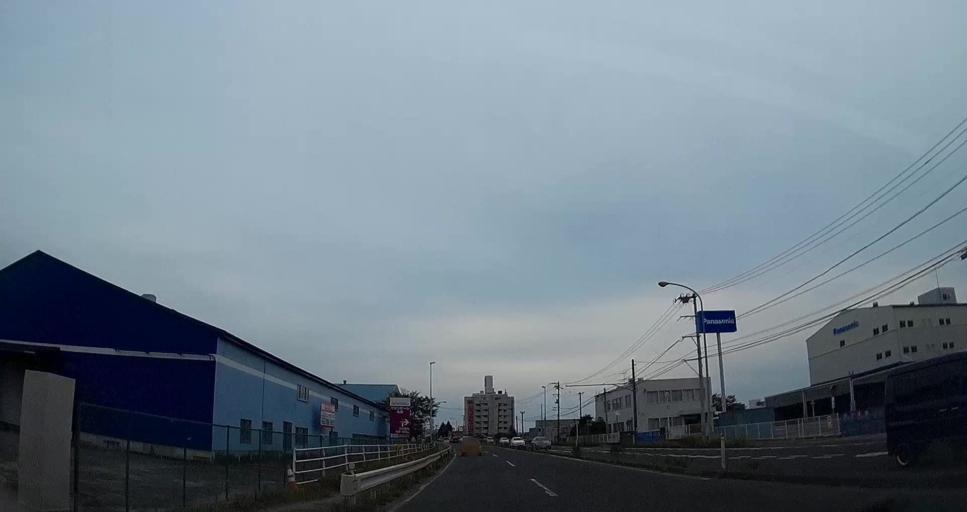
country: JP
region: Miyagi
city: Iwanuma
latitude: 38.1603
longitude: 140.8892
